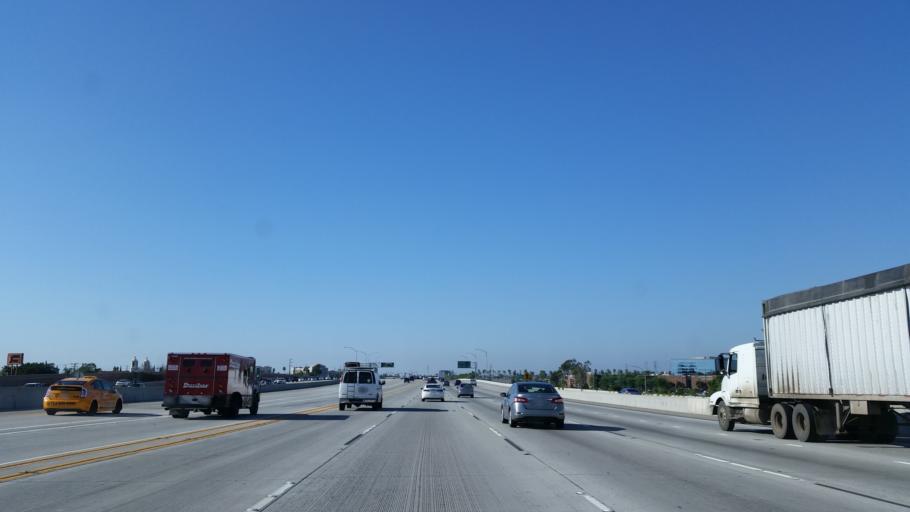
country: US
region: California
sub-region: Orange County
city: Orange
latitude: 33.7929
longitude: -117.8910
